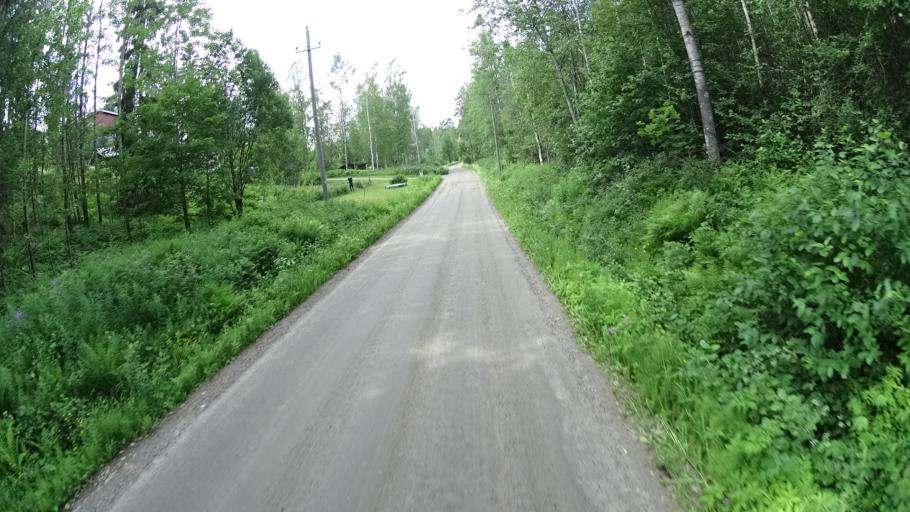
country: FI
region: Uusimaa
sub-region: Helsinki
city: Sibbo
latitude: 60.2765
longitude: 25.3154
